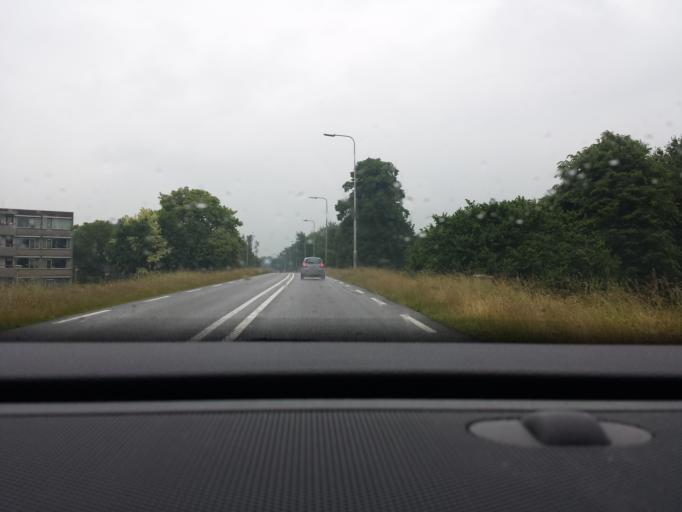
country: NL
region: Overijssel
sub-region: Gemeente Haaksbergen
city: Haaksbergen
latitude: 52.1530
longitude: 6.7491
